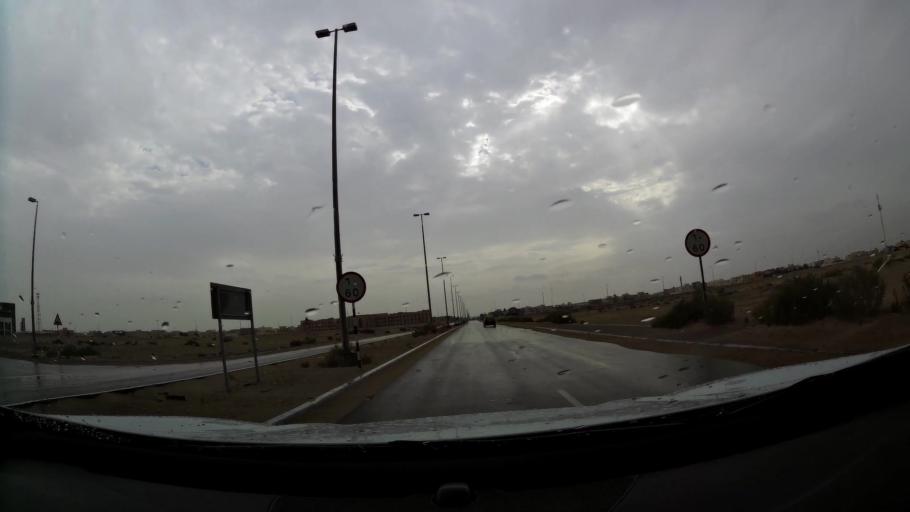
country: AE
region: Abu Dhabi
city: Abu Dhabi
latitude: 24.3657
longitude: 54.6359
